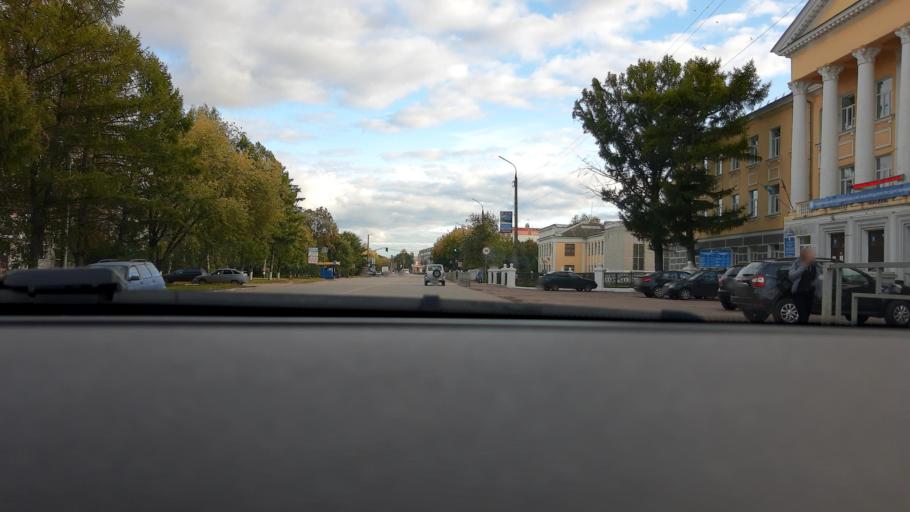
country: RU
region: Nizjnij Novgorod
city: Novaya Balakhna
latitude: 56.5005
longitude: 43.6040
